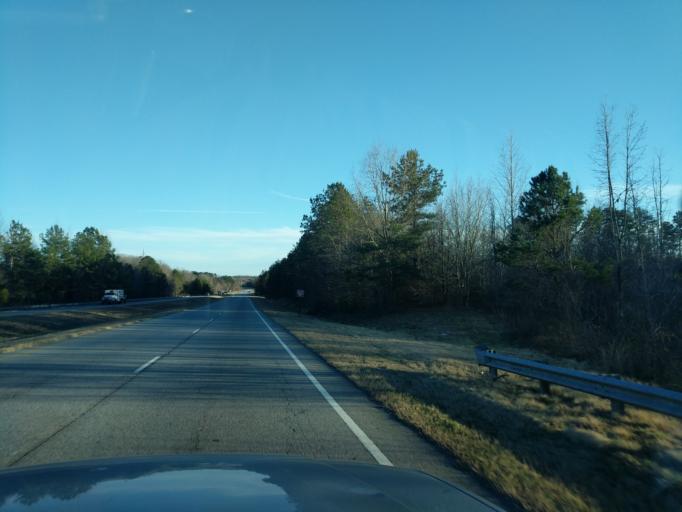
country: US
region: Georgia
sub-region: Stephens County
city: Toccoa
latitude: 34.5499
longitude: -83.3702
